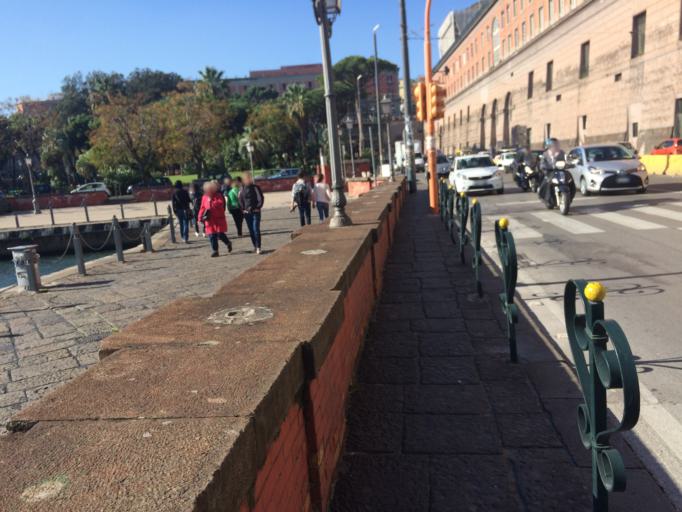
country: IT
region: Campania
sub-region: Provincia di Napoli
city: Napoli
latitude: 40.8365
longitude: 14.2524
